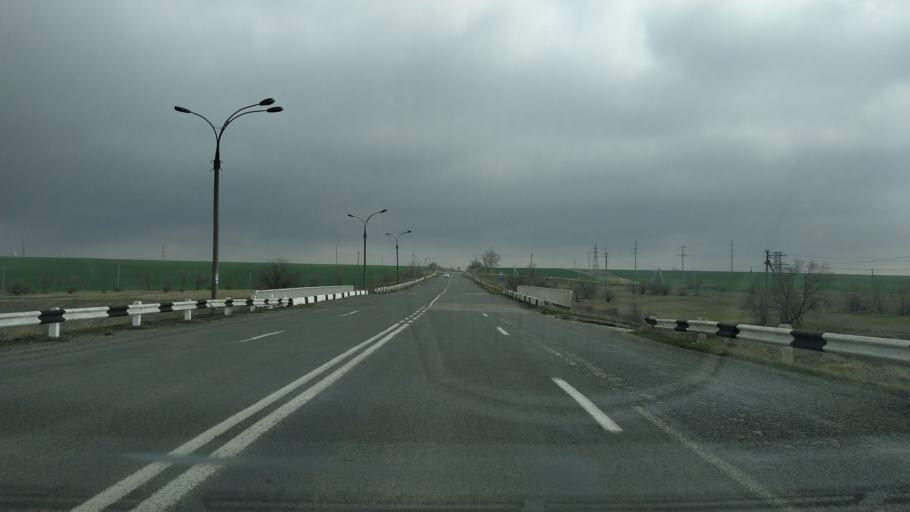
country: MD
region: Straseni
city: Taraclia
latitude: 45.9369
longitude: 28.6176
